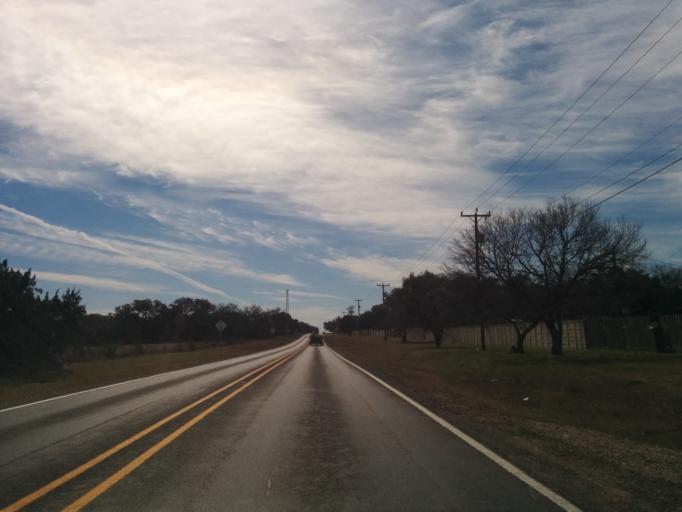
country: US
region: Texas
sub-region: Bexar County
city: Fair Oaks Ranch
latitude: 29.7423
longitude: -98.6233
